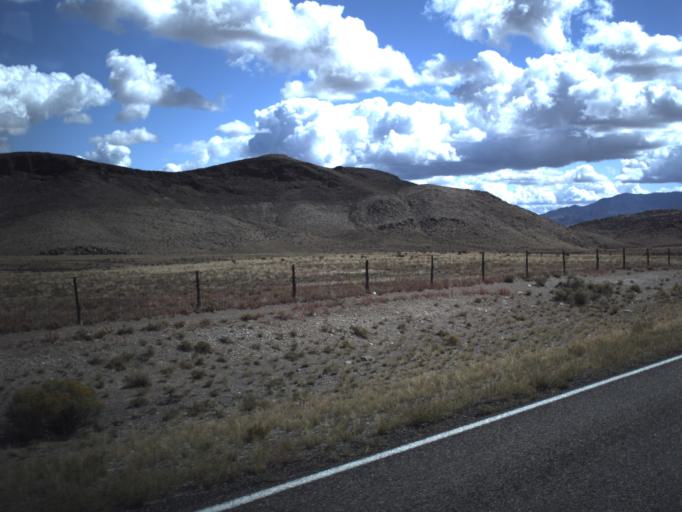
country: US
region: Utah
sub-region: Beaver County
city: Milford
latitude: 38.5942
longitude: -113.8238
